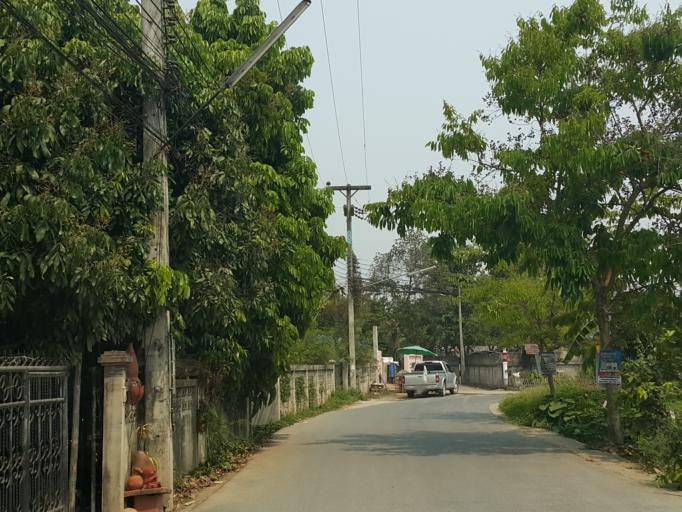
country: TH
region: Chiang Mai
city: Hang Dong
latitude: 18.7232
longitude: 98.9556
